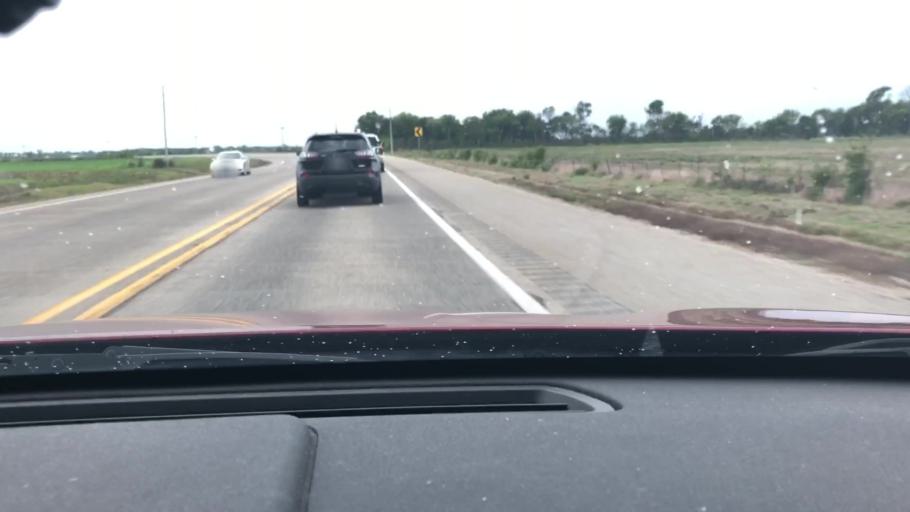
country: US
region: Arkansas
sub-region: Lafayette County
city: Lewisville
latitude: 33.3996
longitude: -93.7446
